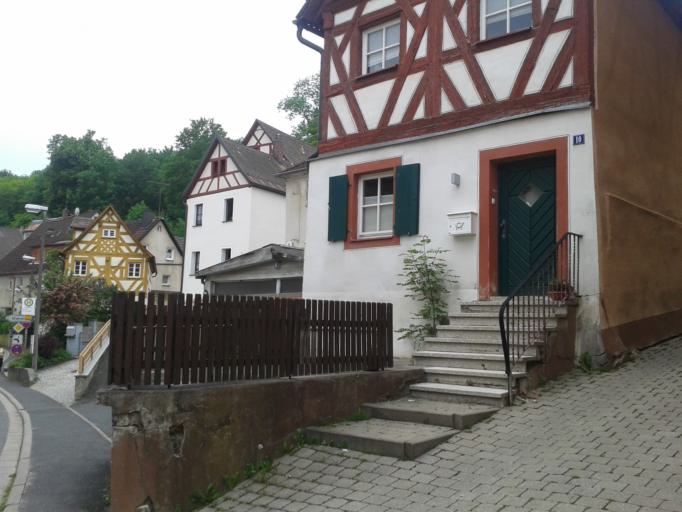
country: DE
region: Bavaria
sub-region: Upper Franconia
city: Grafenberg
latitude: 49.6453
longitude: 11.2486
